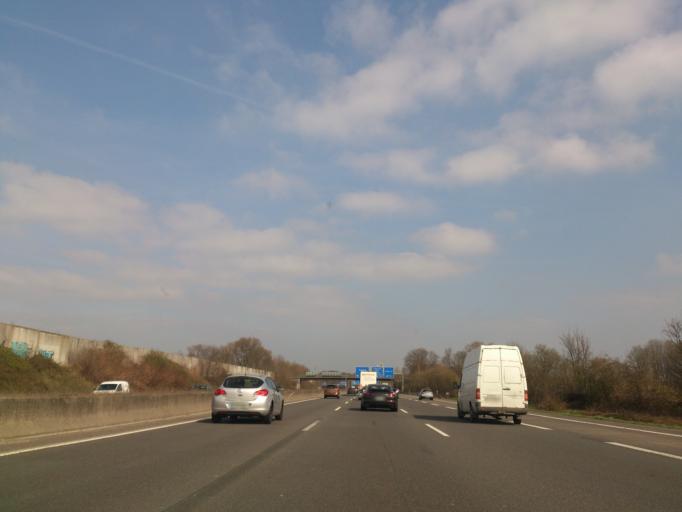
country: DE
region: North Rhine-Westphalia
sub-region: Regierungsbezirk Dusseldorf
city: Hilden
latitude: 51.1927
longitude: 6.9239
